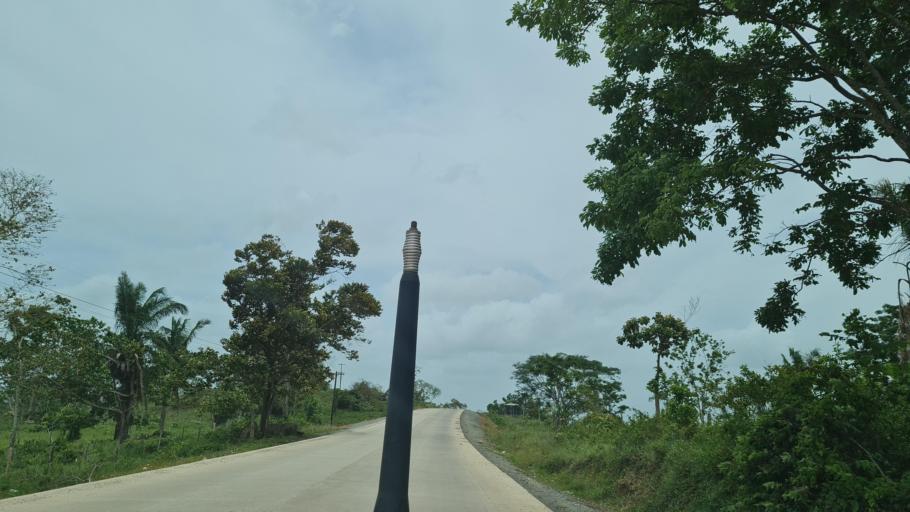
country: NI
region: Atlantico Norte (RAAN)
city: Bonanza
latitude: 14.0439
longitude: -84.0707
